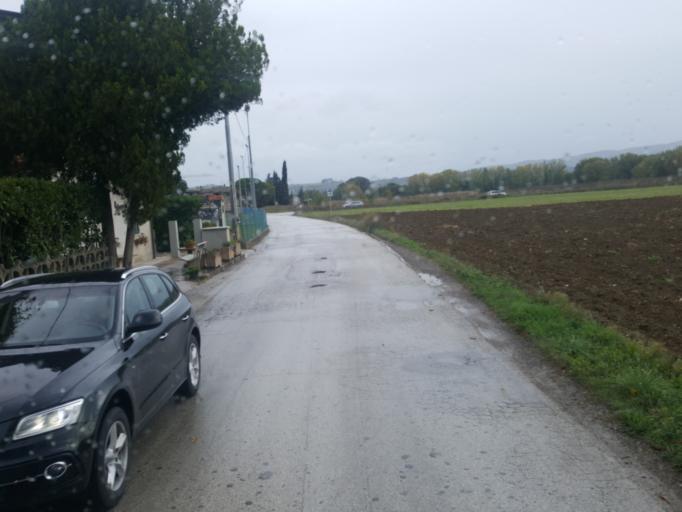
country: IT
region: Umbria
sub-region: Provincia di Perugia
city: San Martino in Campo
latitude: 43.0696
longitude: 12.4225
